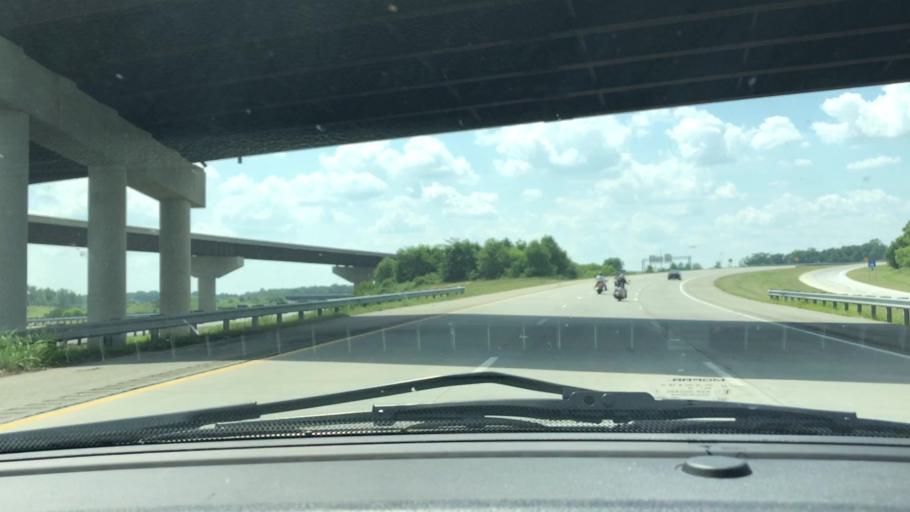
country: US
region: North Carolina
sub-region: Guilford County
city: Greensboro
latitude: 36.0034
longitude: -79.8459
